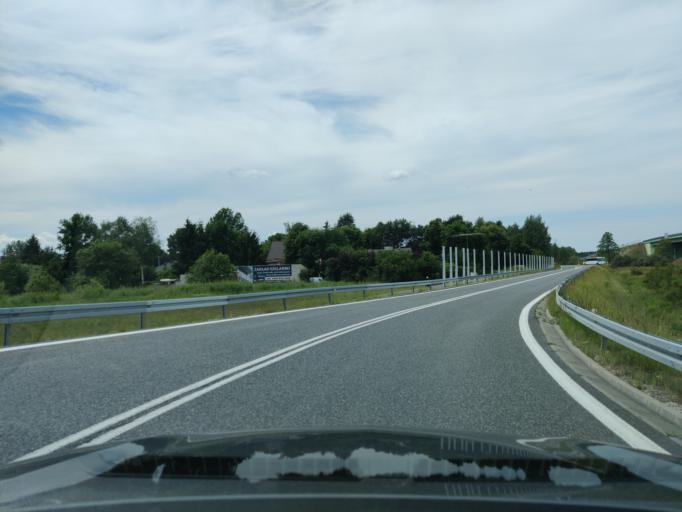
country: PL
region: Masovian Voivodeship
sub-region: Powiat wyszkowski
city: Wyszkow
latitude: 52.5568
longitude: 21.4638
